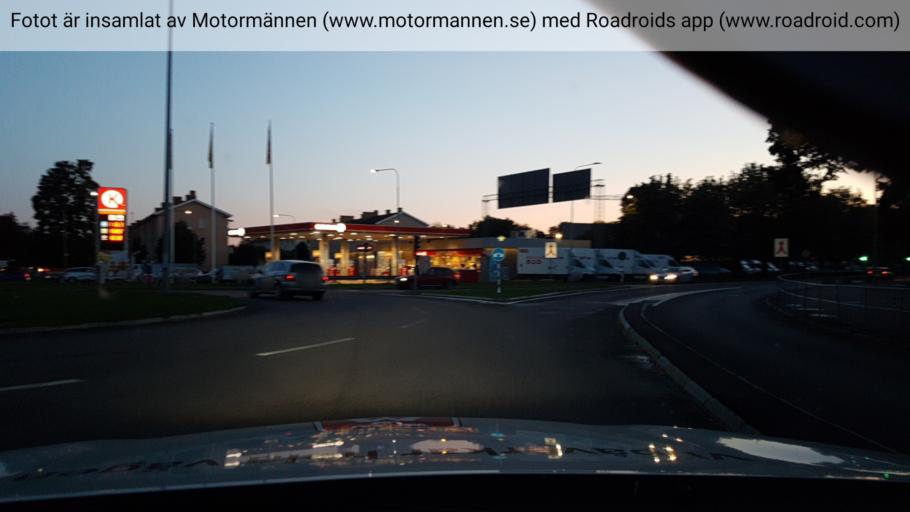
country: SE
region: Vaermland
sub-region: Karlstads Kommun
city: Karlstad
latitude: 59.3943
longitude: 13.5165
